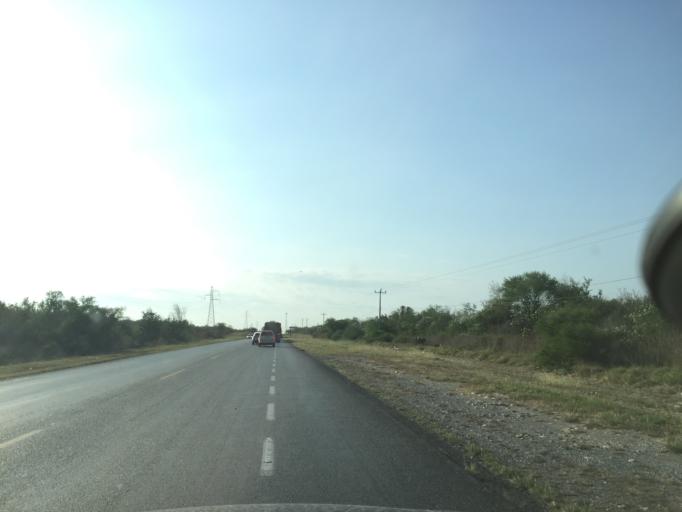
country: MX
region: Tamaulipas
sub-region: Hidalgo
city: Estacion Santa Engracia
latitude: 24.1410
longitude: -99.2705
